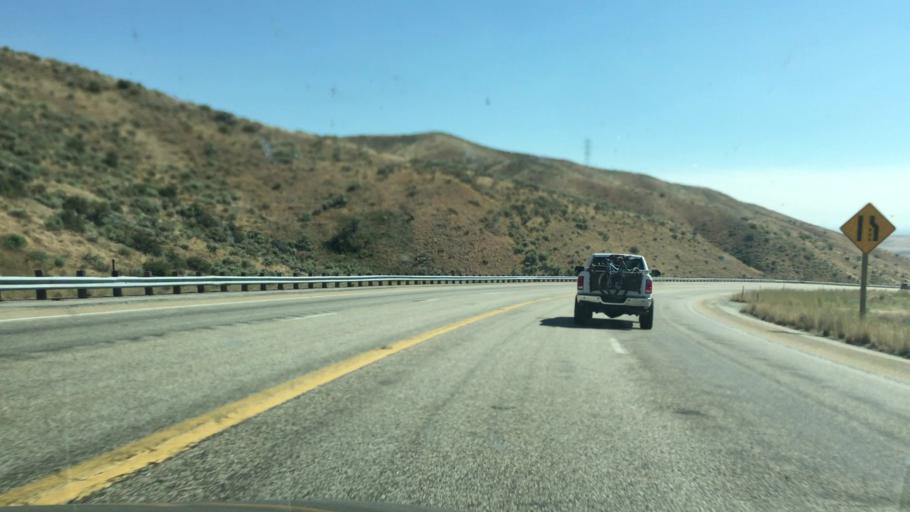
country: US
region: Idaho
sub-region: Ada County
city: Eagle
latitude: 43.8318
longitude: -116.2447
